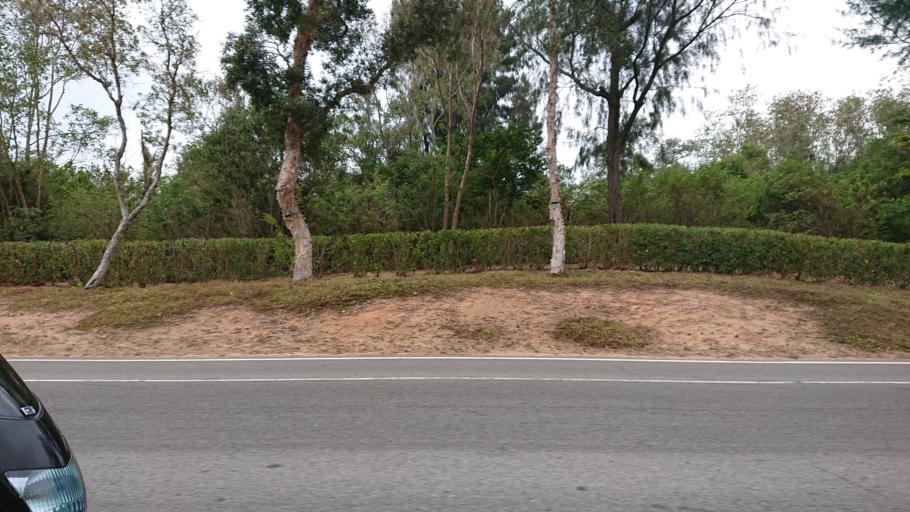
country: TW
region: Fukien
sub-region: Kinmen
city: Jincheng
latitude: 24.4387
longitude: 118.3997
